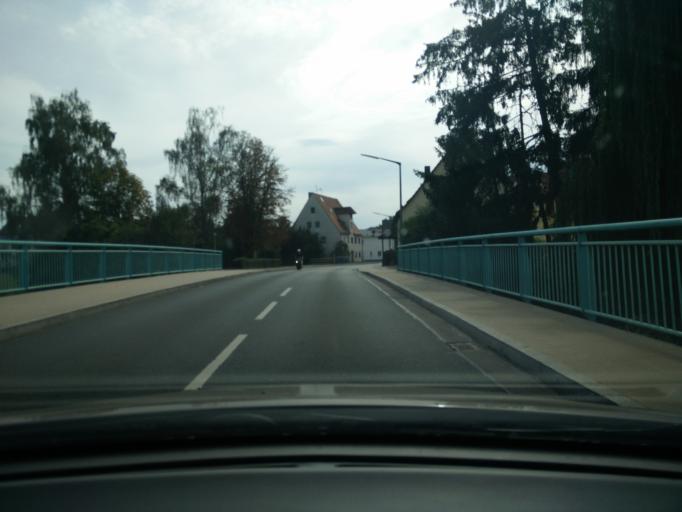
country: DE
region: Bavaria
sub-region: Regierungsbezirk Mittelfranken
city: Veitsbronn
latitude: 49.5103
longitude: 10.8796
